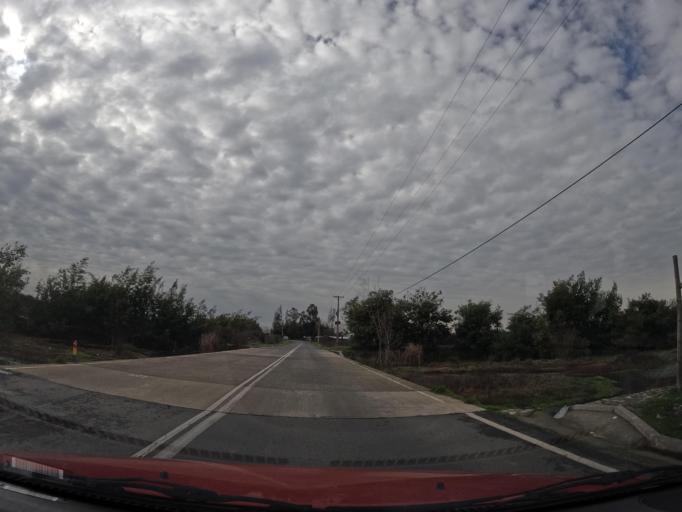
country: CL
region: Maule
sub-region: Provincia de Linares
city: Linares
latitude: -35.8639
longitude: -71.6189
